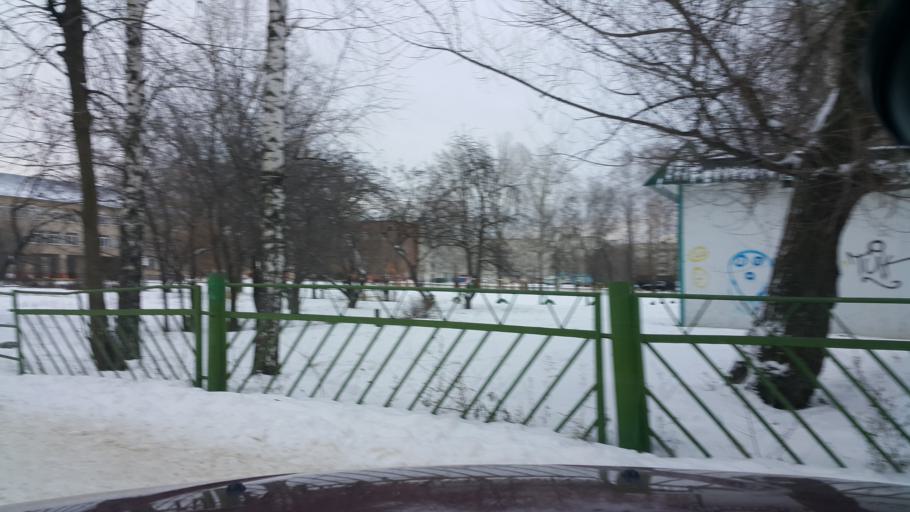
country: RU
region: Tambov
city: Bokino
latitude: 52.6523
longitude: 41.4481
